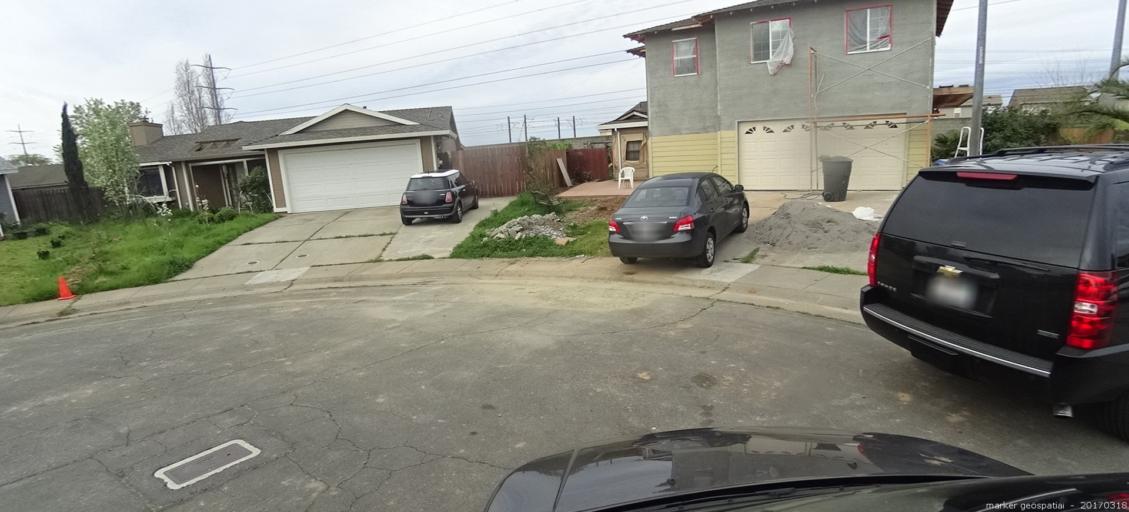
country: US
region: California
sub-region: Sacramento County
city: Parkway
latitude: 38.4862
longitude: -121.4670
